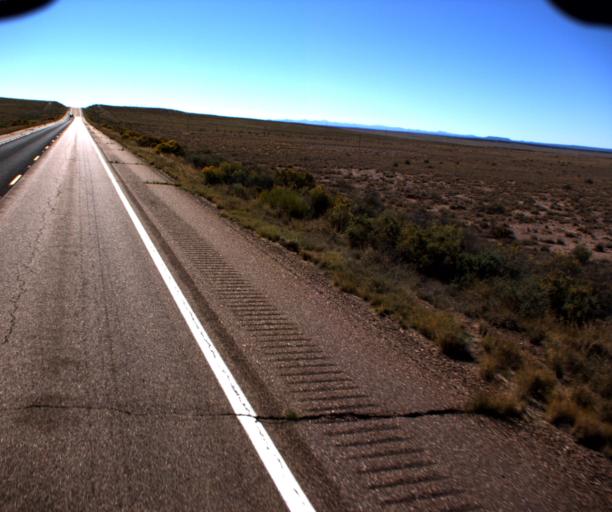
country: US
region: Arizona
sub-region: Navajo County
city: Snowflake
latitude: 34.7580
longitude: -109.8090
